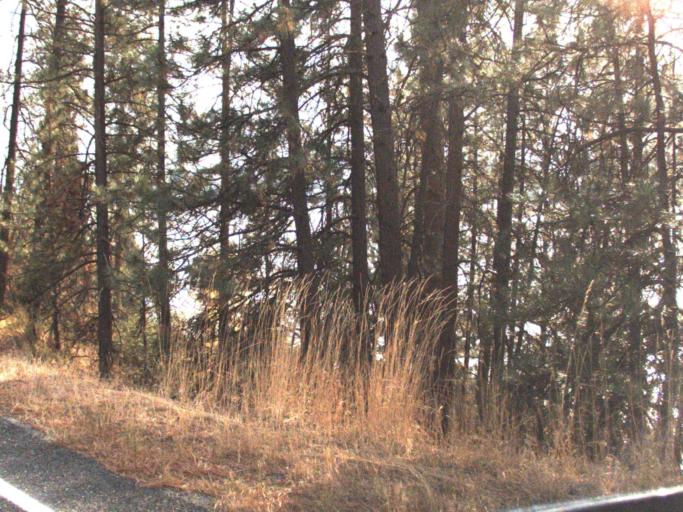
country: US
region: Washington
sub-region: Stevens County
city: Kettle Falls
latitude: 48.3203
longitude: -118.1503
